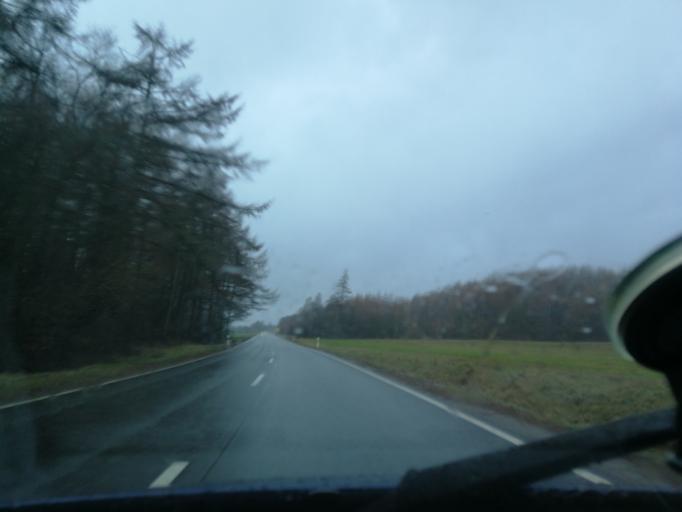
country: DE
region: Rheinland-Pfalz
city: Gielert
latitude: 49.7648
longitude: 6.9983
